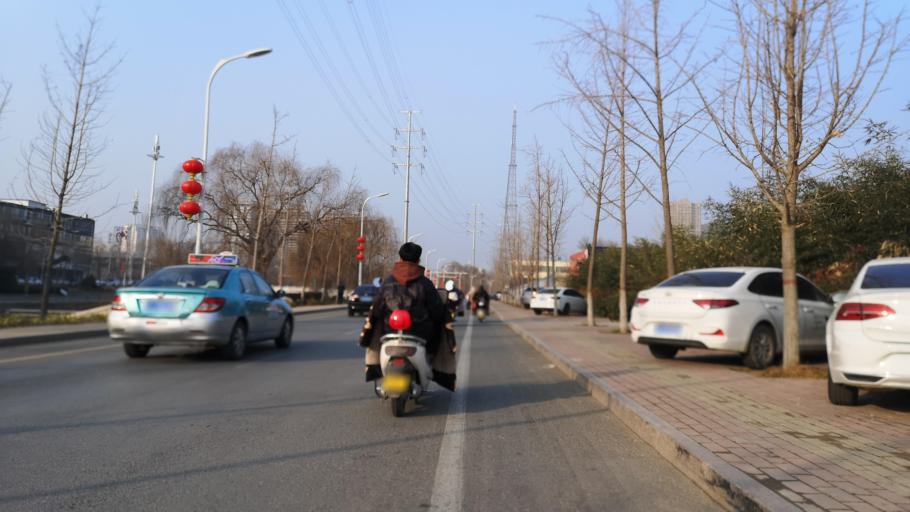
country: CN
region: Henan Sheng
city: Zhongyuanlu
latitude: 35.7740
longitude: 115.0487
